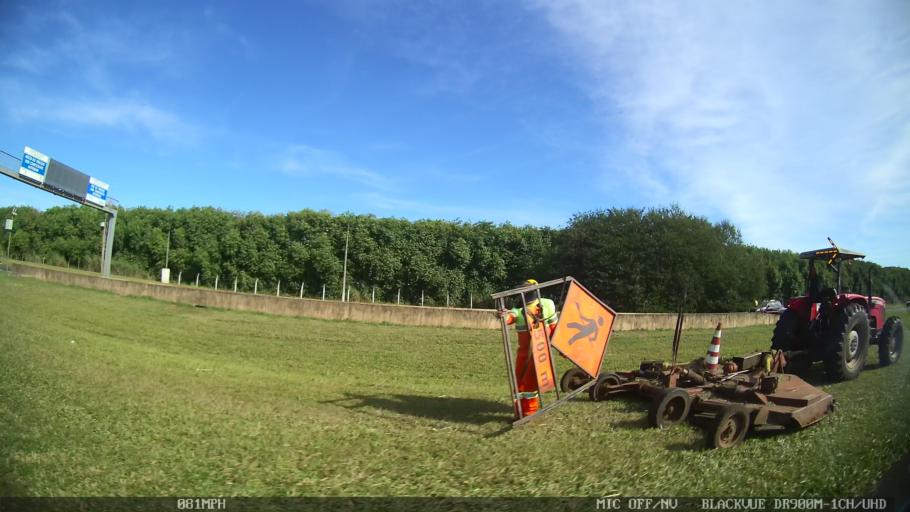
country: BR
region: Sao Paulo
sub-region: Cordeiropolis
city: Cordeiropolis
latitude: -22.4557
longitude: -47.3990
